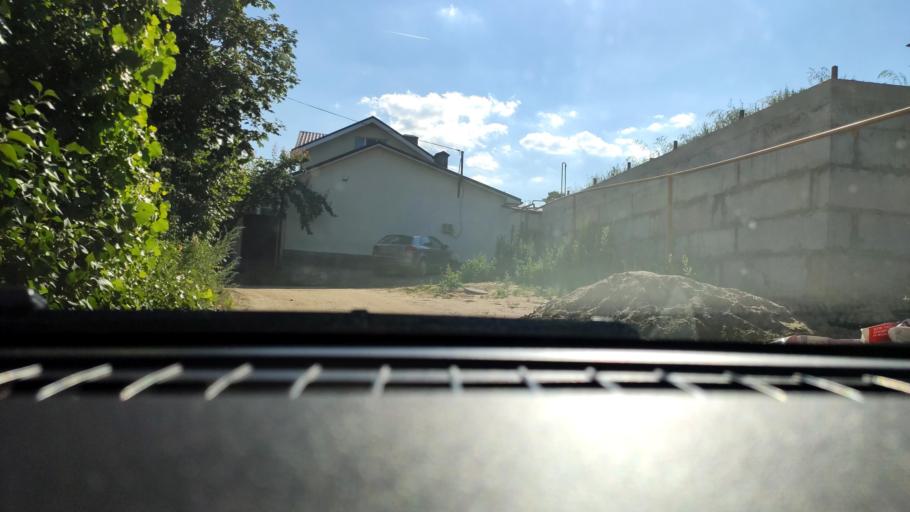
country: RU
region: Voronezj
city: Ramon'
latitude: 51.8152
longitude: 39.2683
